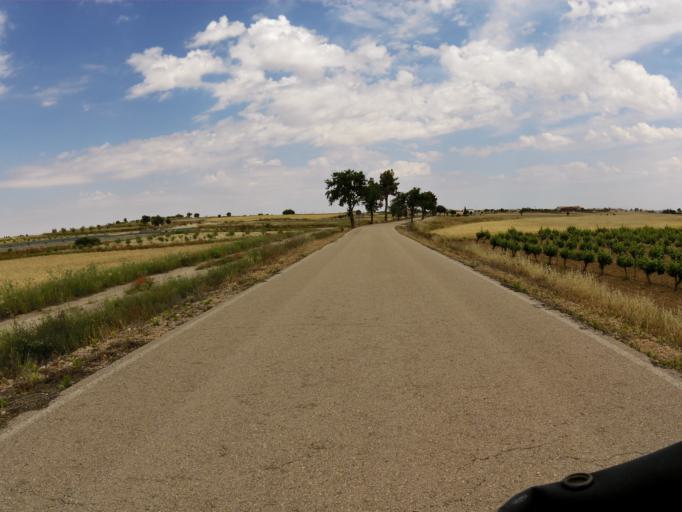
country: ES
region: Castille-La Mancha
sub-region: Provincia de Albacete
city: Valdeganga
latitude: 39.1171
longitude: -1.6840
